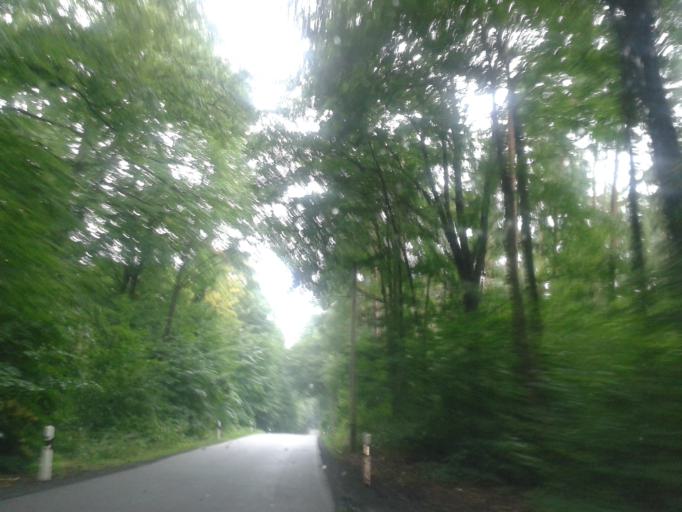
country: DE
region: Saxony
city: Radebeul
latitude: 51.1113
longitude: 13.7000
